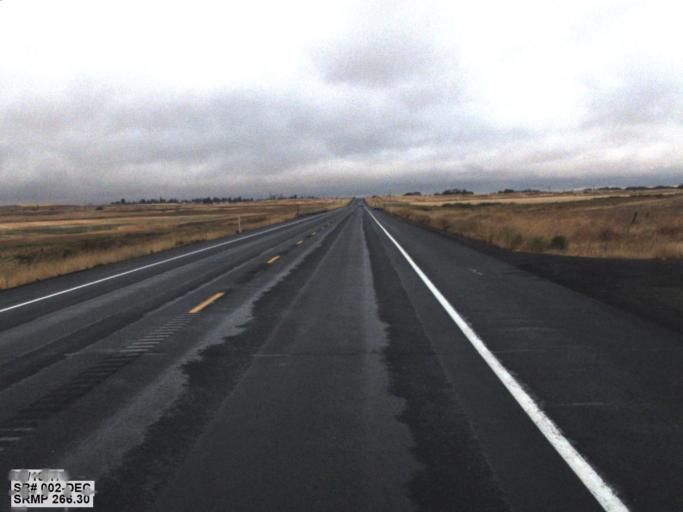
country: US
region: Washington
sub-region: Spokane County
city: Medical Lake
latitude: 47.6604
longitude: -117.8304
